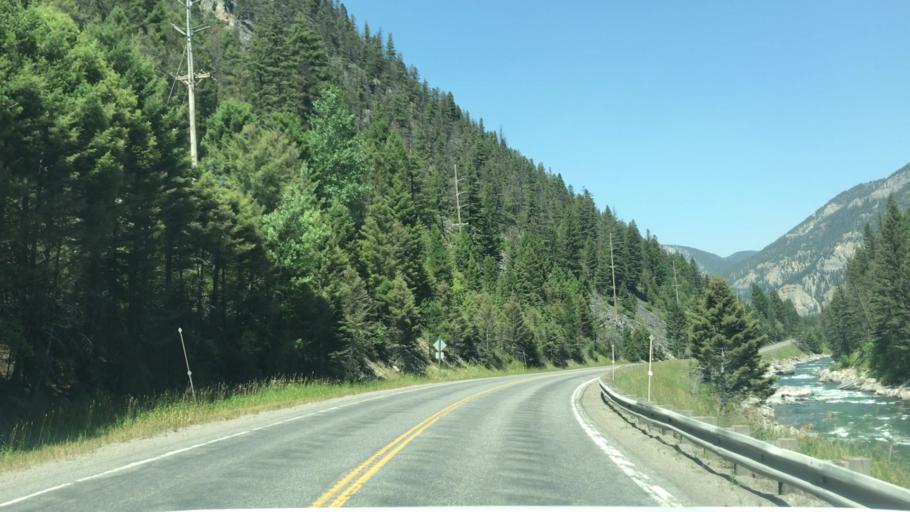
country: US
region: Montana
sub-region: Gallatin County
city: Big Sky
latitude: 45.4220
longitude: -111.2341
